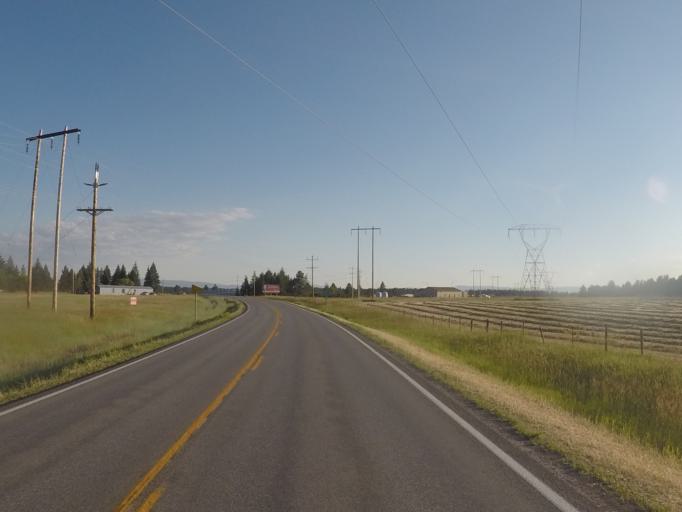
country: US
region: Montana
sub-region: Flathead County
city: Columbia Falls
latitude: 48.3582
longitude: -114.1564
